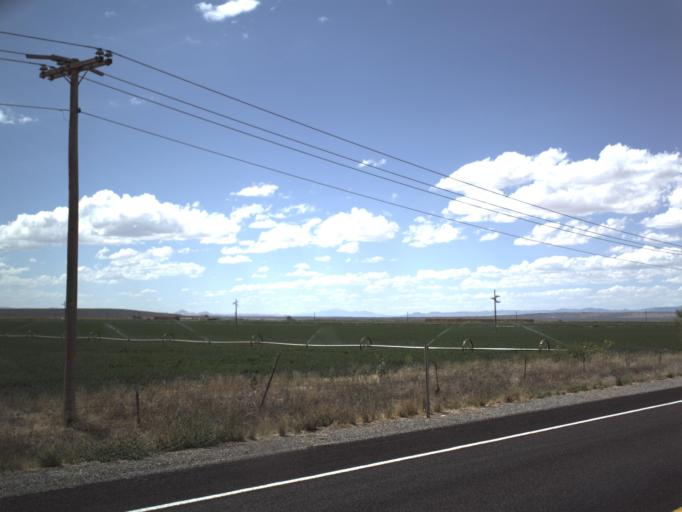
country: US
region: Utah
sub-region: Millard County
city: Fillmore
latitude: 39.1181
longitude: -112.3429
